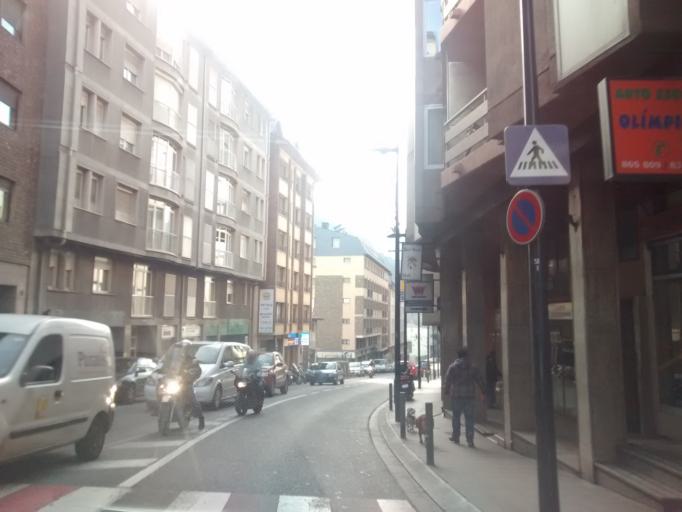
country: AD
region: Andorra la Vella
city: Andorra la Vella
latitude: 42.5028
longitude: 1.5134
